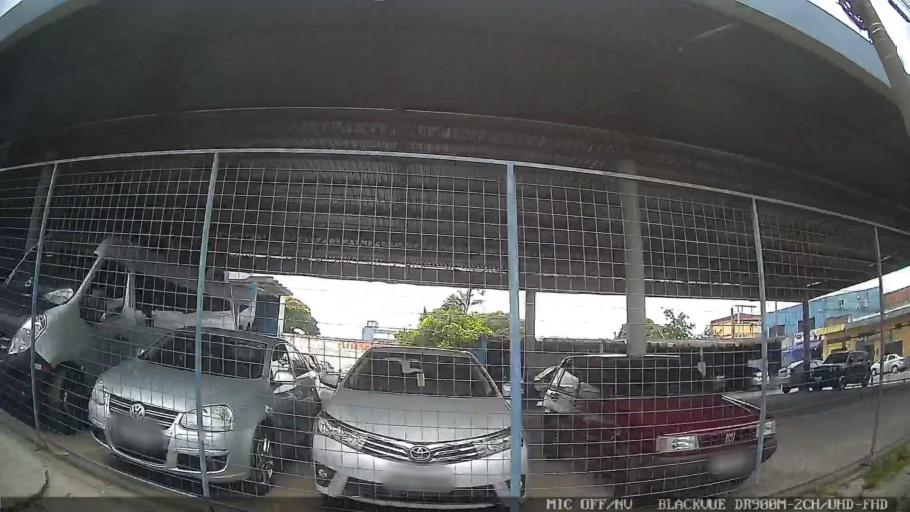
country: BR
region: Sao Paulo
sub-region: Suzano
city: Suzano
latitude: -23.5339
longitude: -46.3100
